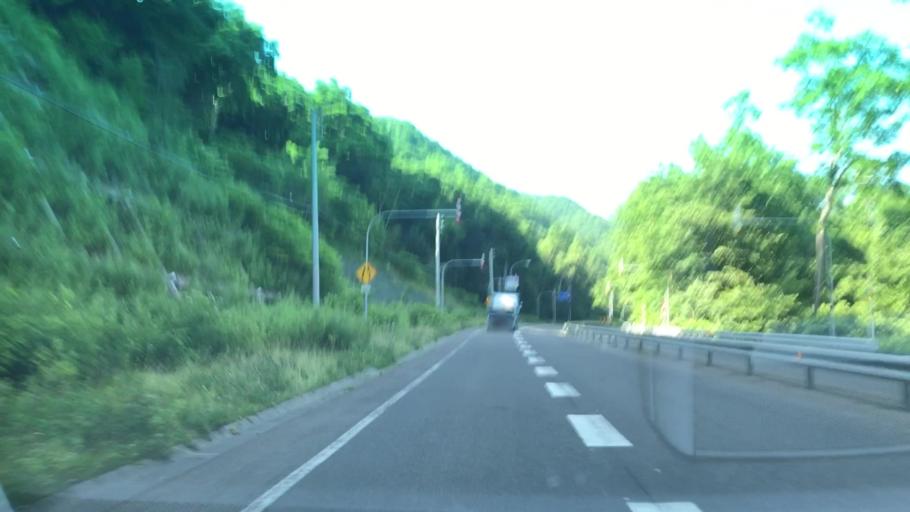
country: JP
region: Hokkaido
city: Iwanai
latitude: 43.0169
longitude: 140.6664
